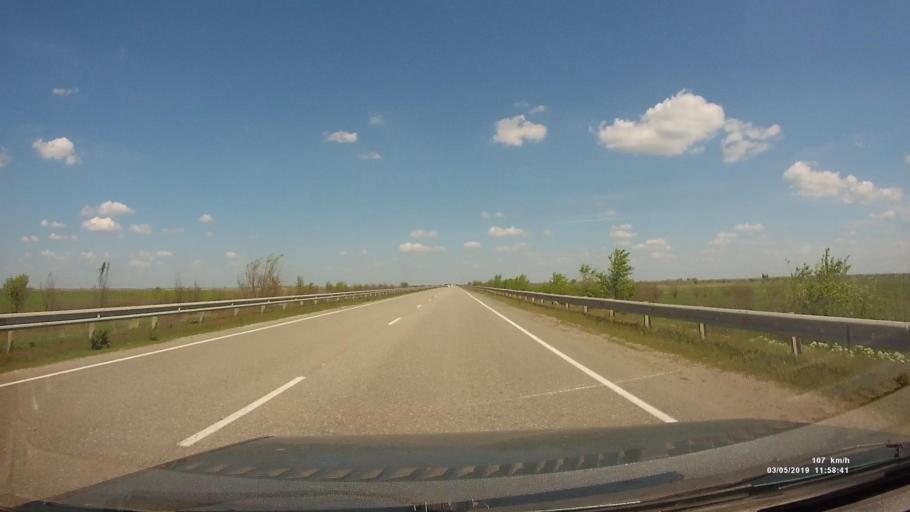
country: RU
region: Rostov
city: Bagayevskaya
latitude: 47.2241
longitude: 40.3225
